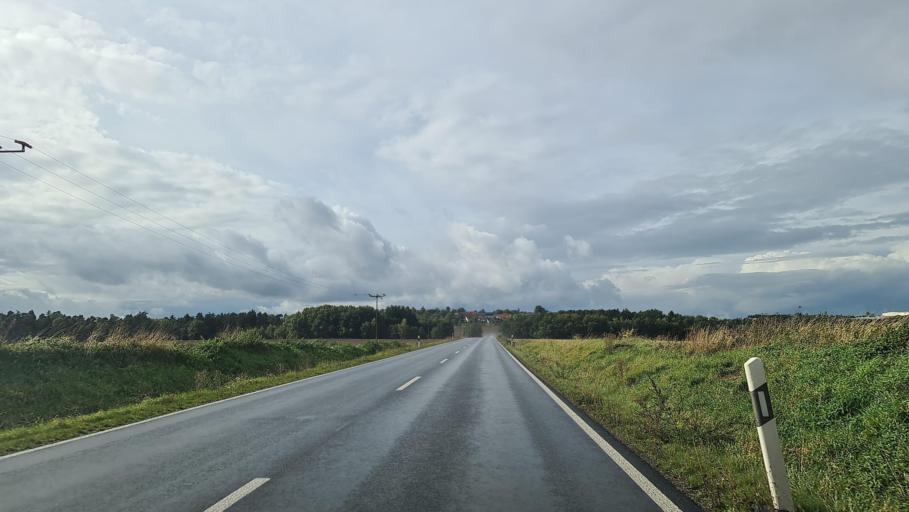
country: DE
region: Thuringia
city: Hohenolsen
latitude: 50.7320
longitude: 12.0989
